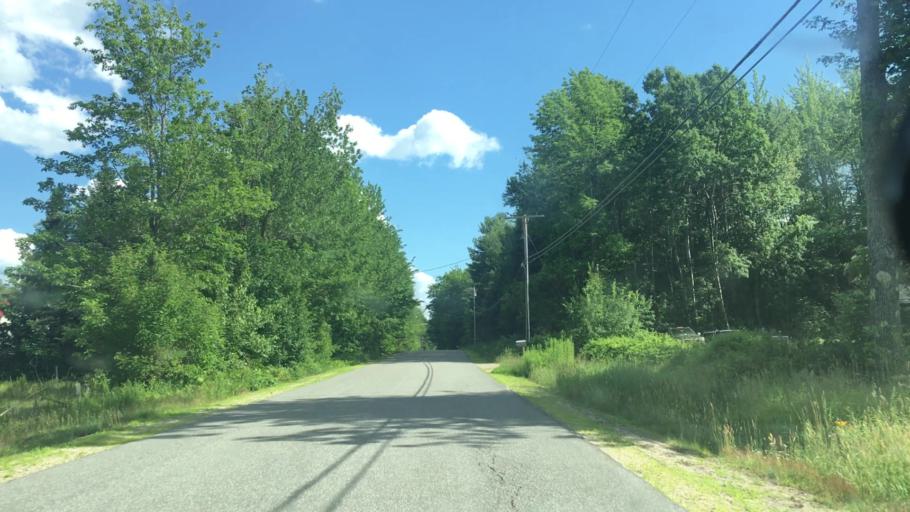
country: US
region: Maine
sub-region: Franklin County
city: Wilton
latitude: 44.6382
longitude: -70.1997
